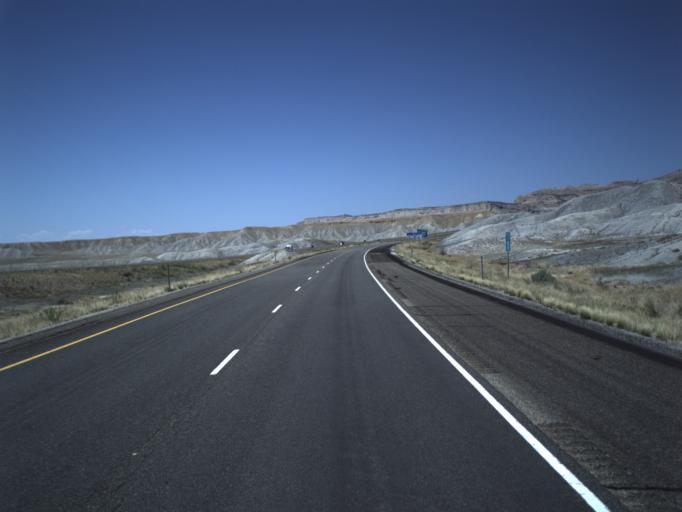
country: US
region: Utah
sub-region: Grand County
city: Moab
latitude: 38.9521
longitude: -109.6958
